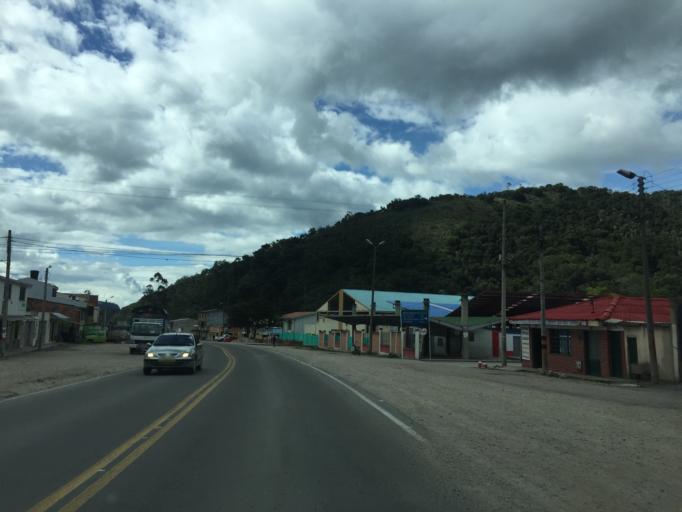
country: CO
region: Boyaca
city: Arcabuco
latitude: 5.7549
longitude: -73.4351
